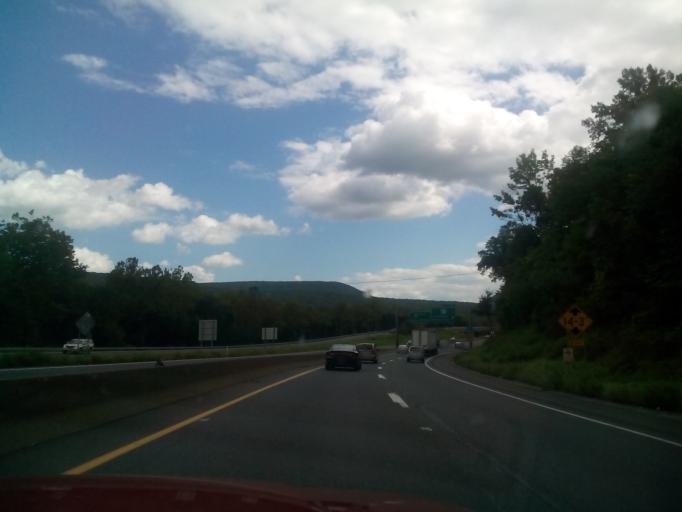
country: US
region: Pennsylvania
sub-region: Monroe County
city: East Stroudsburg
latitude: 40.9967
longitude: -75.1442
